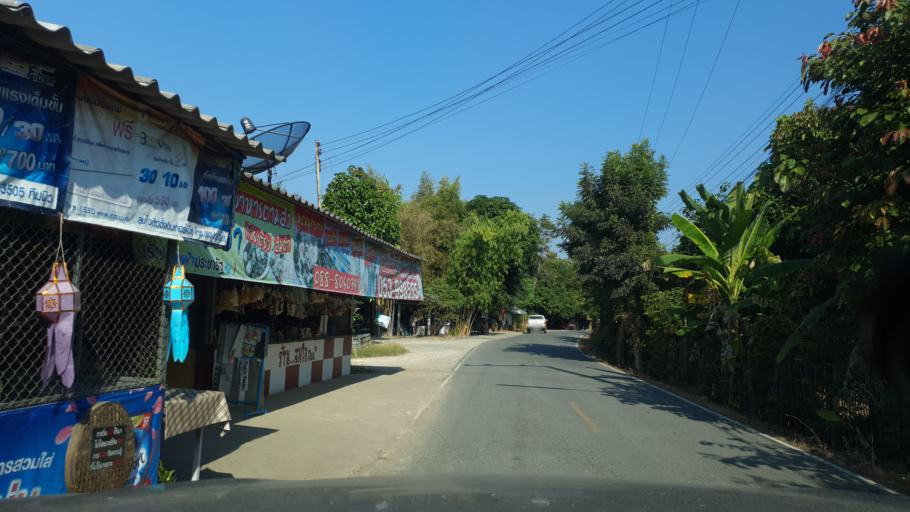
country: TH
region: Chiang Mai
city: Saraphi
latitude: 18.7022
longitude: 99.0766
